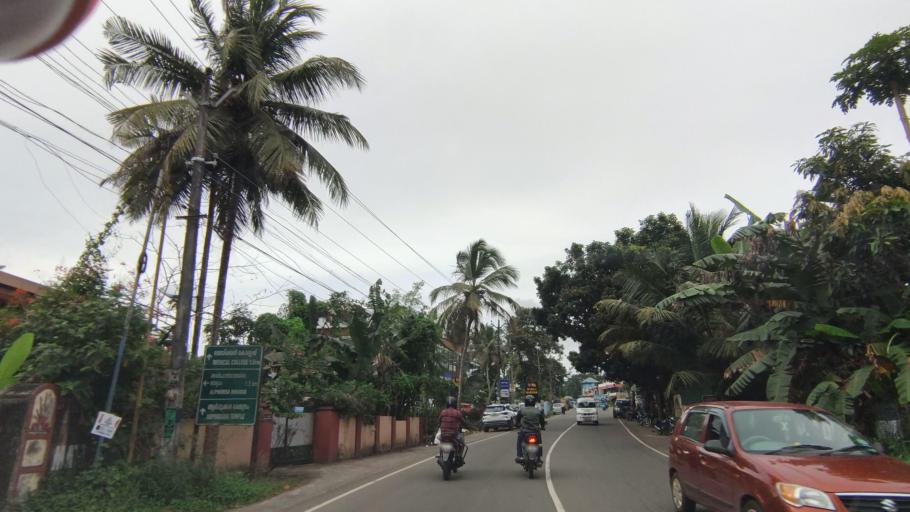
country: IN
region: Kerala
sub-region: Kottayam
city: Kottayam
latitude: 9.6272
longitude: 76.5122
